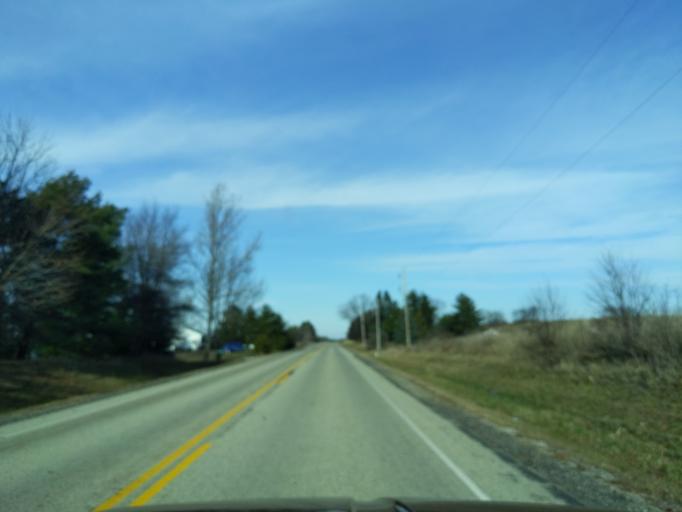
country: US
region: Wisconsin
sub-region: Jefferson County
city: Palmyra
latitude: 42.7868
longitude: -88.6024
